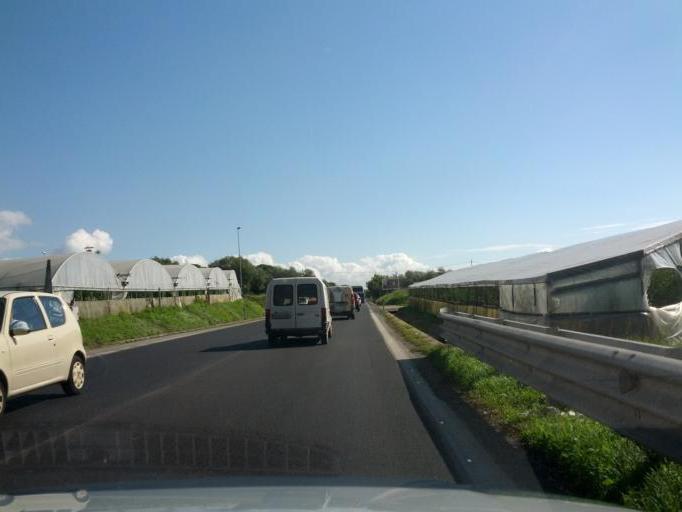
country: IT
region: Latium
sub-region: Provincia di Latina
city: Formia
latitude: 41.2677
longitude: 13.6436
